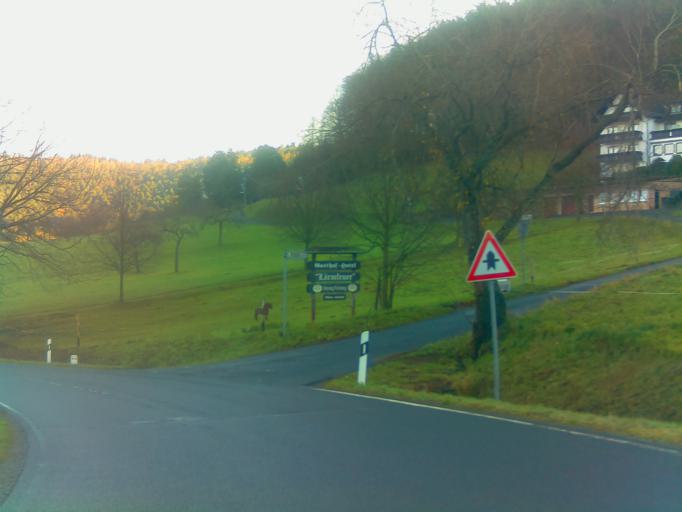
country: DE
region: Hesse
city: Reichelsheim
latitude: 49.6752
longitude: 8.8876
